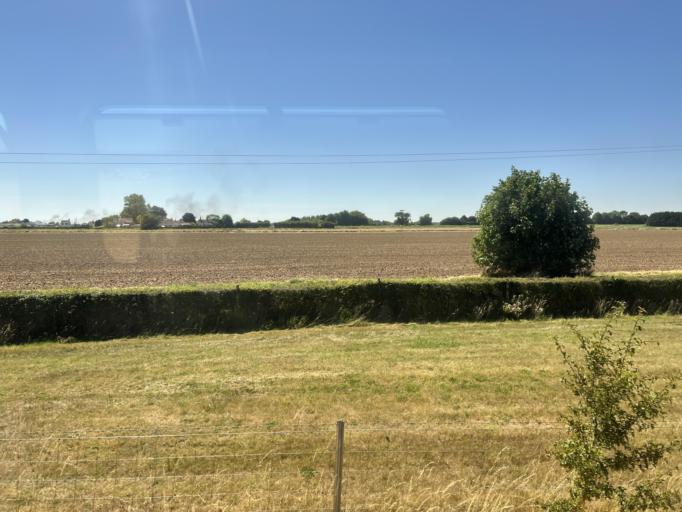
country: GB
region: England
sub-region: Lincolnshire
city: Wainfleet All Saints
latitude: 53.1104
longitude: 0.2232
